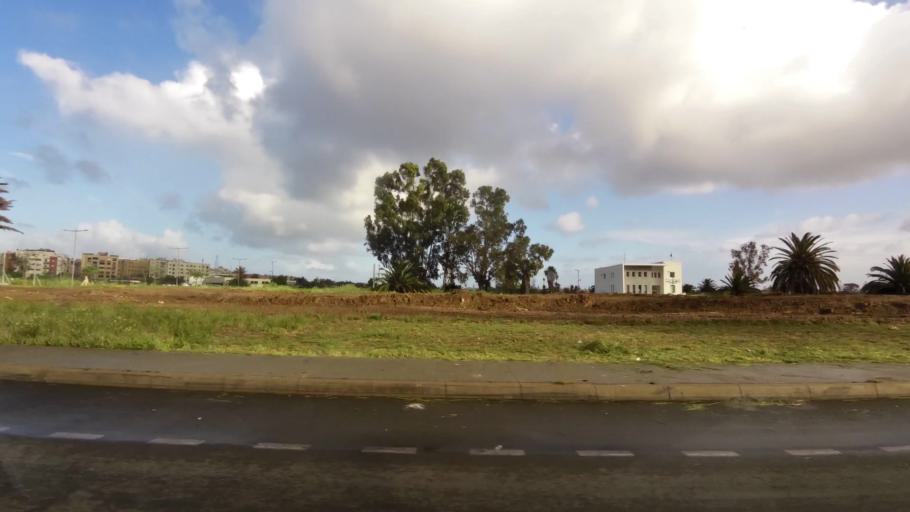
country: MA
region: Grand Casablanca
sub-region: Casablanca
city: Casablanca
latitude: 33.5638
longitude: -7.6641
